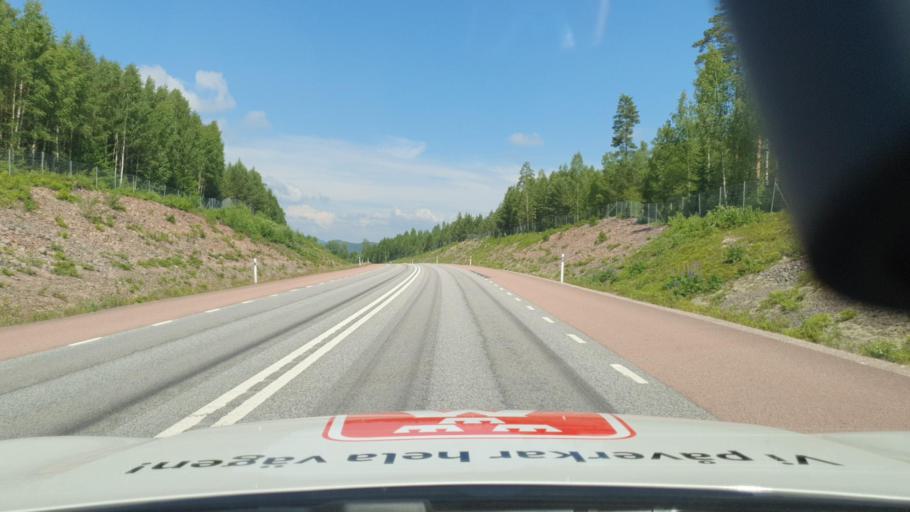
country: SE
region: Vaermland
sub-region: Torsby Kommun
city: Torsby
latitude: 60.1943
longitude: 13.0223
